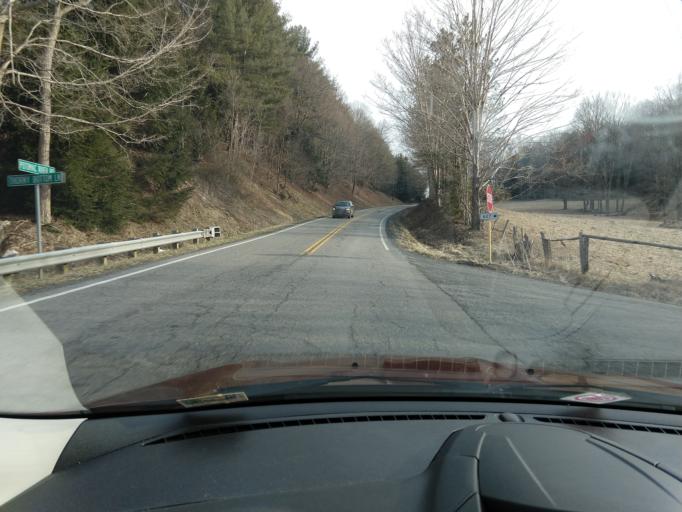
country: US
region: Virginia
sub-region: Highland County
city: Monterey
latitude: 38.4542
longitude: -79.5313
